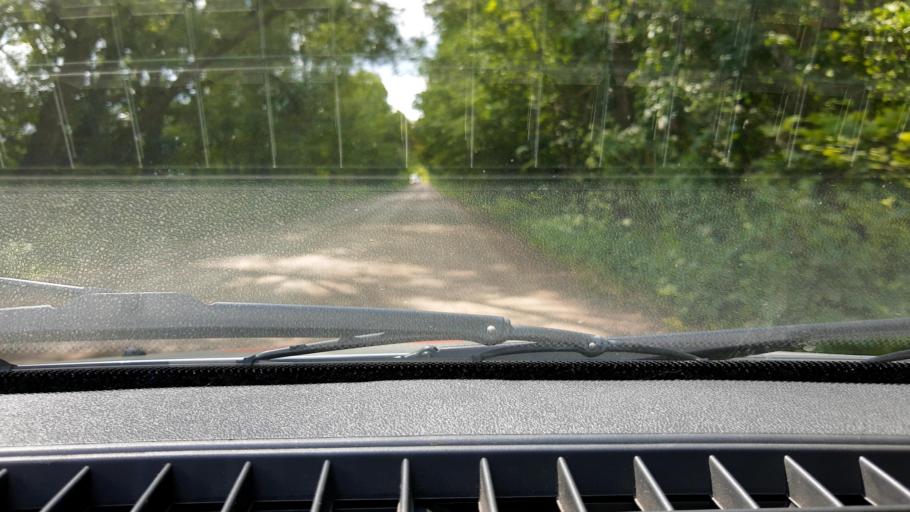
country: RU
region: Bashkortostan
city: Ufa
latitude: 54.6814
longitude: 56.0607
